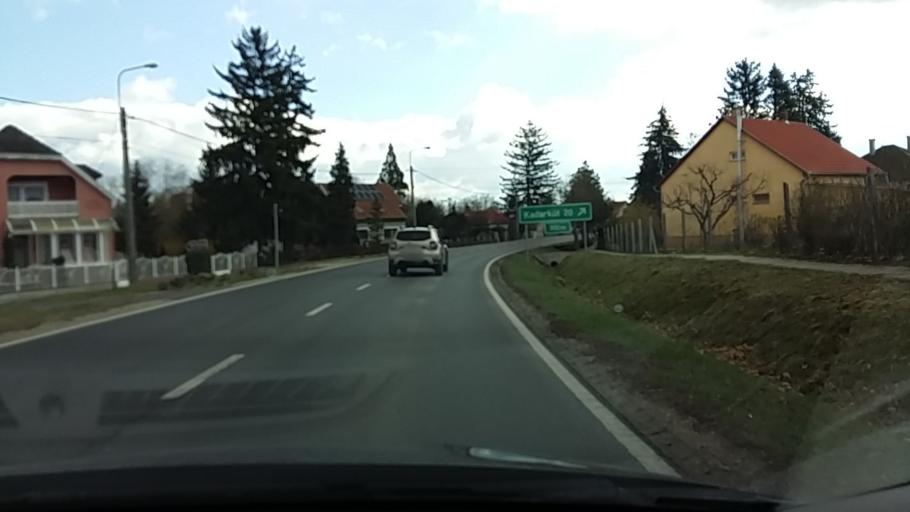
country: HU
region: Somogy
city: Nagybajom
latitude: 46.3893
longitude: 17.5151
